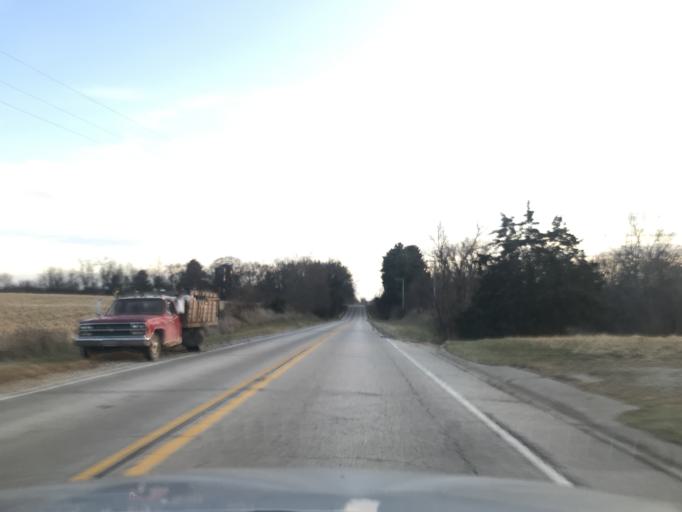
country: US
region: Illinois
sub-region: Henderson County
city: Oquawka
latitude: 40.9386
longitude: -90.8641
